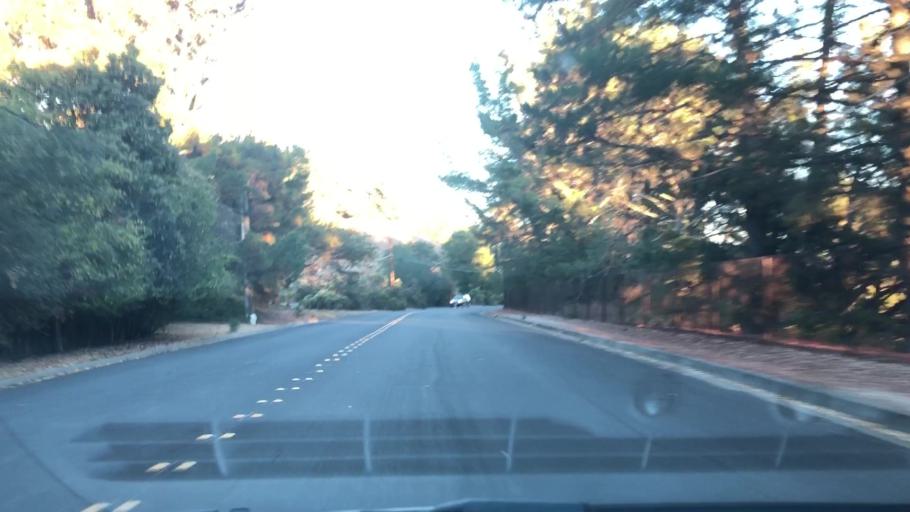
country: US
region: California
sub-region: Contra Costa County
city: Orinda
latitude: 37.8938
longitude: -122.1626
